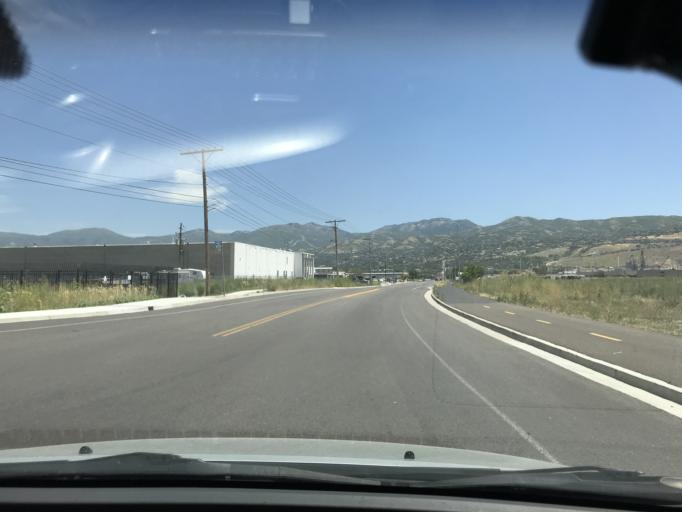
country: US
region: Utah
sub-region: Davis County
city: North Salt Lake
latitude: 40.8419
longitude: -111.9395
